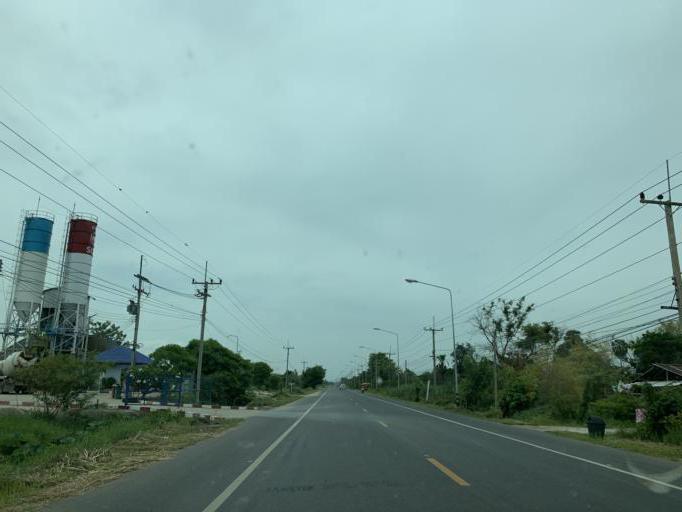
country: TH
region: Nakhon Sawan
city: Lat Yao
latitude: 15.7610
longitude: 99.7464
